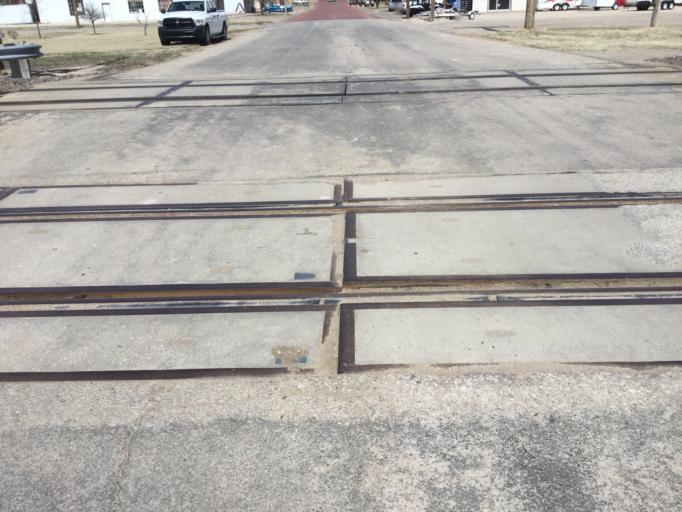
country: US
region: Kansas
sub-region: Trego County
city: WaKeeney
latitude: 39.0234
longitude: -99.8824
